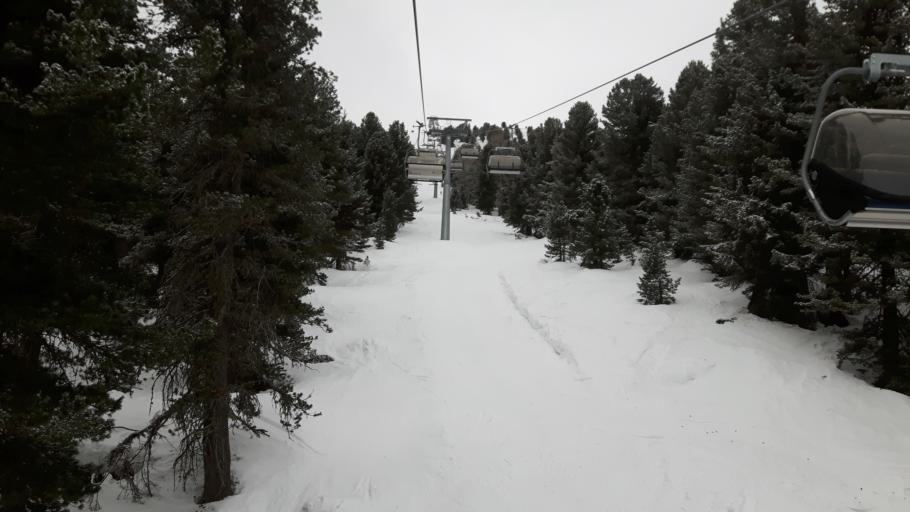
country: IT
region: Trentino-Alto Adige
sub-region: Provincia di Trento
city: Panchia
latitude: 46.3493
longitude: 11.5391
